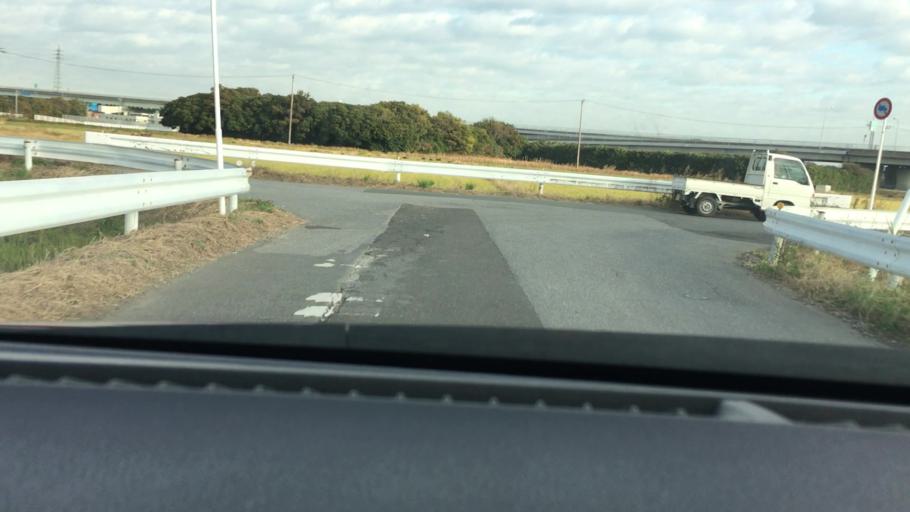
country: JP
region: Chiba
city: Kisarazu
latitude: 35.4071
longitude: 139.9601
